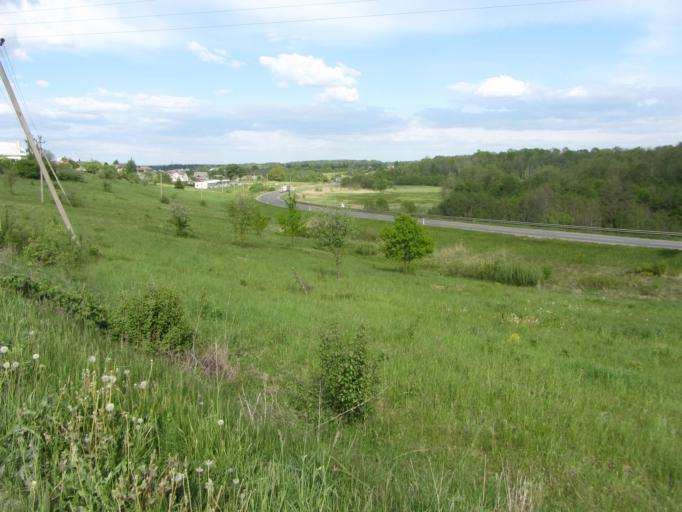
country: LT
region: Utenos apskritis
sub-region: Utena
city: Utena
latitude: 55.4818
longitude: 25.5908
